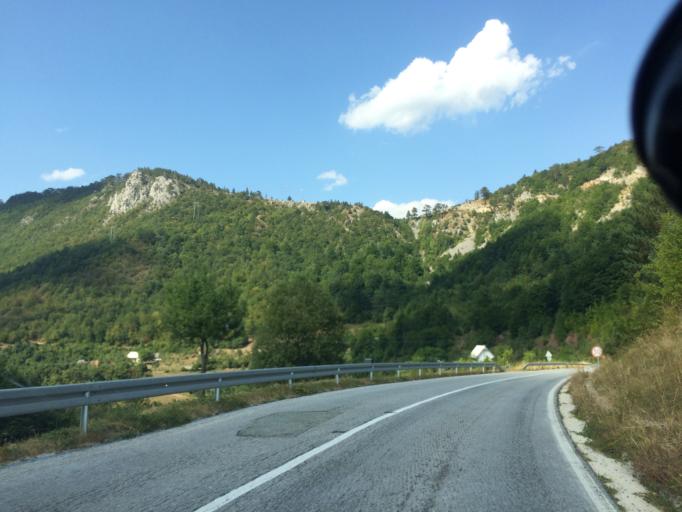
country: ME
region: Opstina Zabljak
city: Zabljak
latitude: 43.1587
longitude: 19.3062
